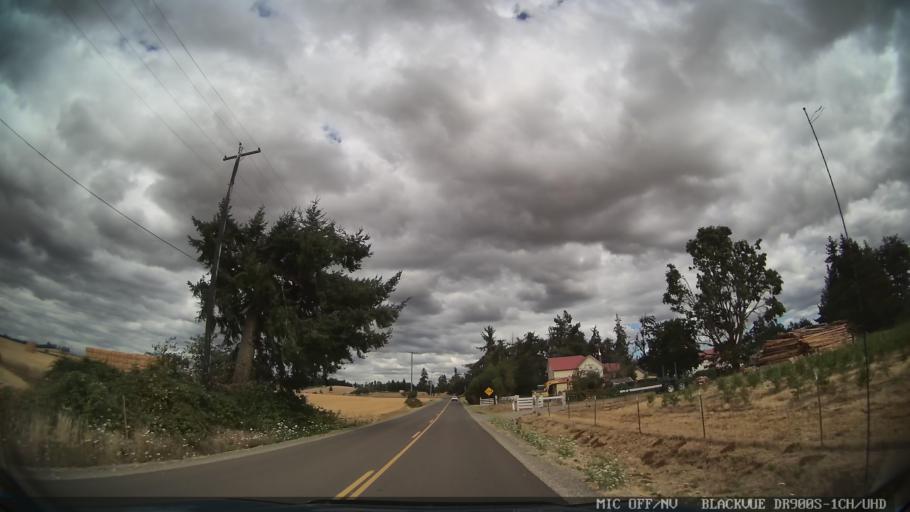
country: US
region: Oregon
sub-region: Marion County
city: Sublimity
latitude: 44.8661
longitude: -122.7597
